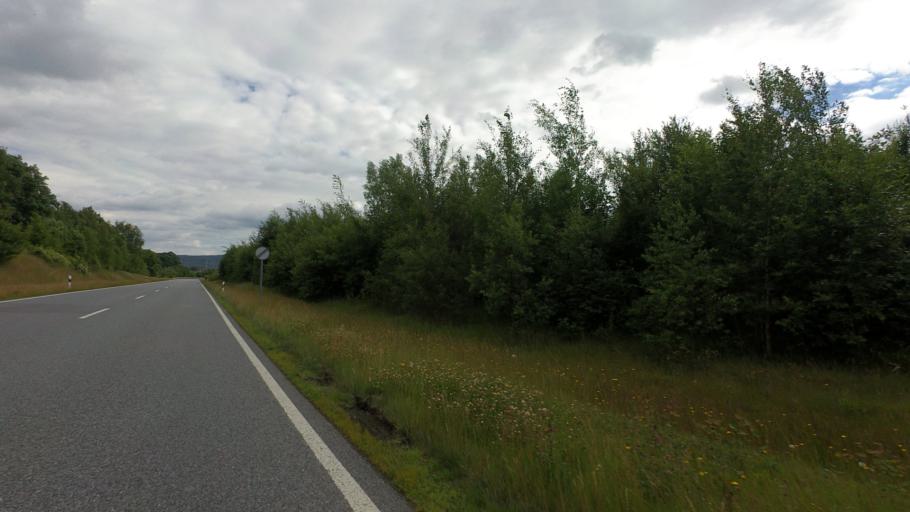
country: DE
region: Saxony
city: Berthelsdorf
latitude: 51.0454
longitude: 14.2126
